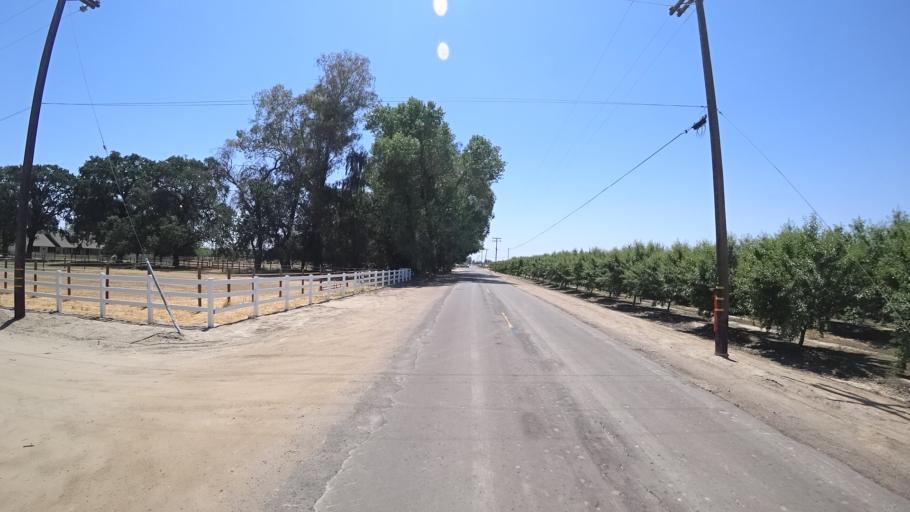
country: US
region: California
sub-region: Kings County
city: Lemoore
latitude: 36.2854
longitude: -119.7628
